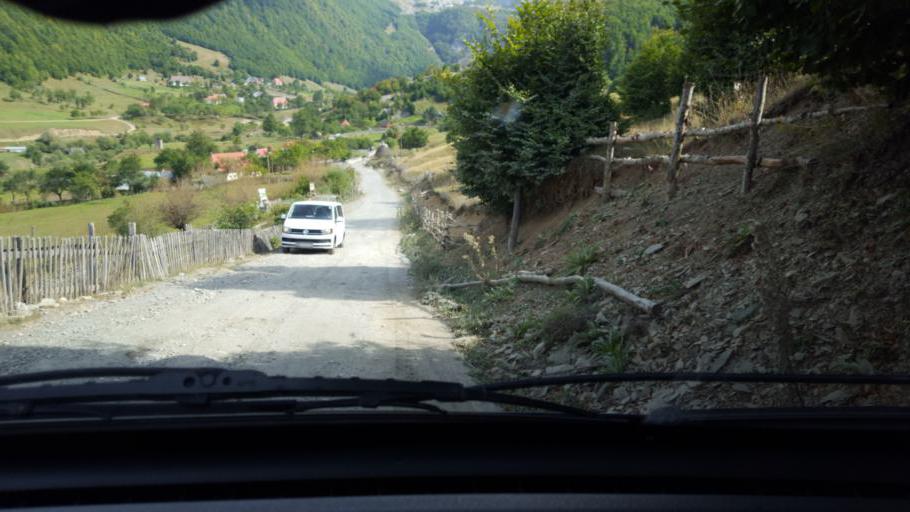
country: AL
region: Kukes
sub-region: Rrethi i Tropojes
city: Valbone
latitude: 42.5303
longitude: 19.7237
